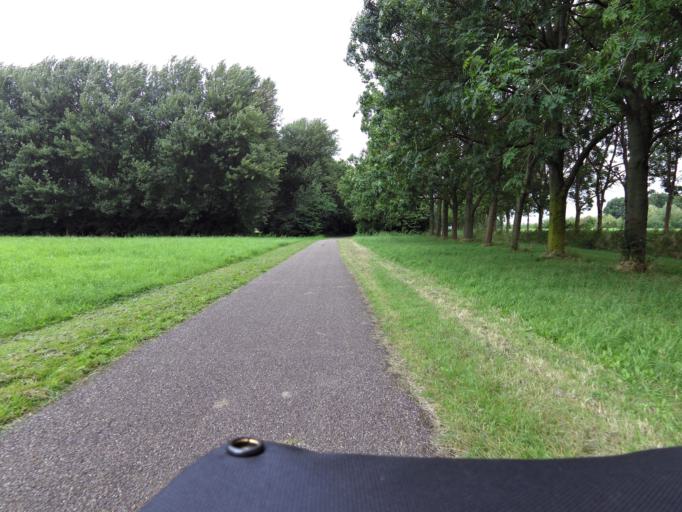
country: NL
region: South Holland
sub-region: Gemeente Spijkenisse
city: Spijkenisse
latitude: 51.8293
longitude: 4.2593
